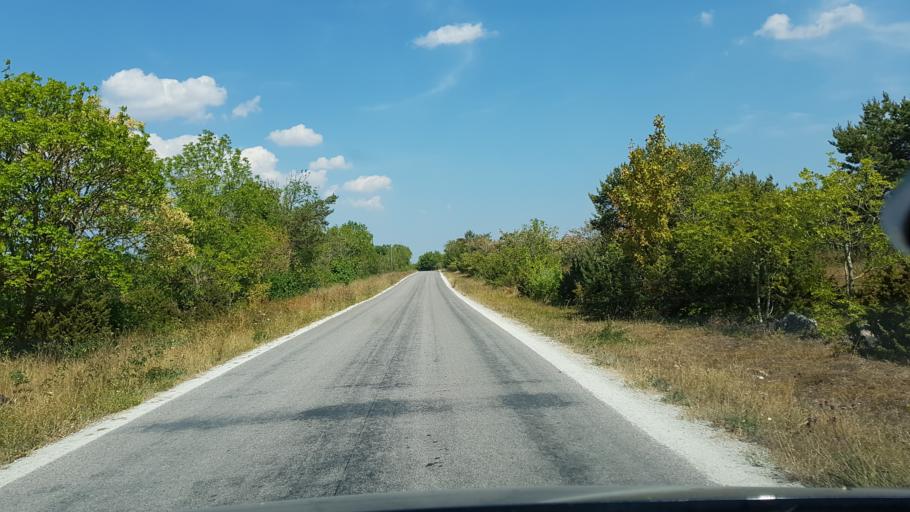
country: SE
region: Gotland
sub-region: Gotland
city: Visby
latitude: 57.6546
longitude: 18.3591
